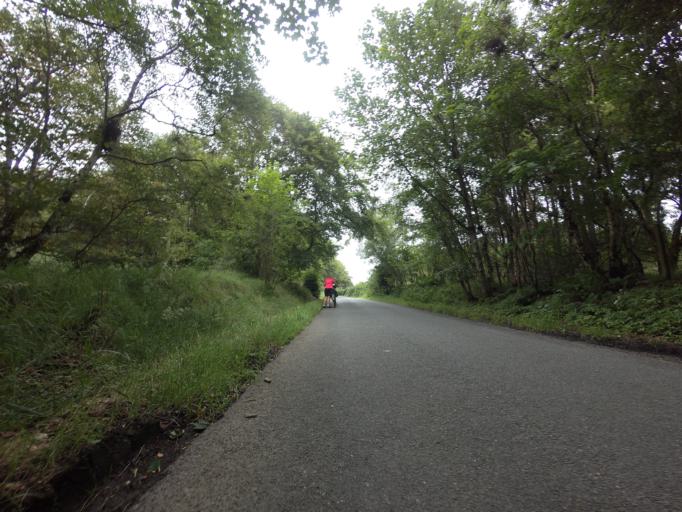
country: GB
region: Scotland
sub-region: Aberdeenshire
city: Turriff
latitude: 57.5349
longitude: -2.4106
